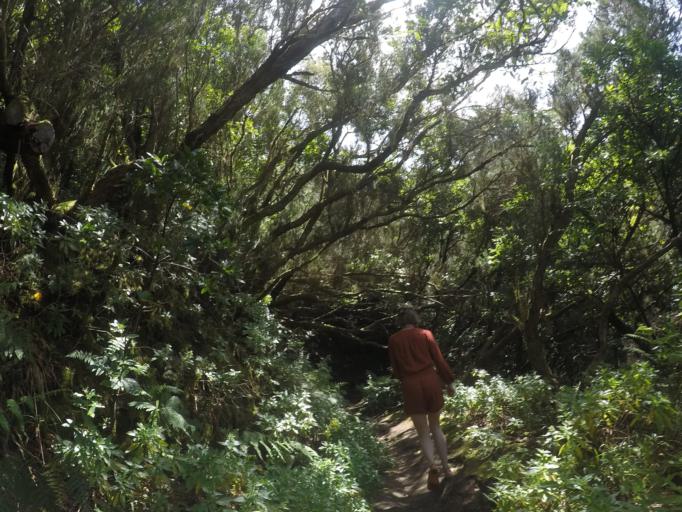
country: ES
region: Canary Islands
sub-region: Provincia de Santa Cruz de Tenerife
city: Santa Cruz de Tenerife
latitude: 28.5435
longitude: -16.2262
